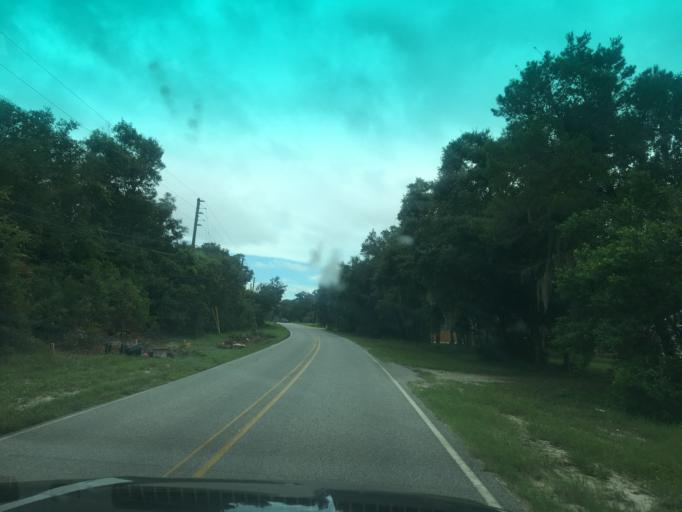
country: US
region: Florida
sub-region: Wakulla County
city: Crawfordville
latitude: 29.9125
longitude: -84.3658
